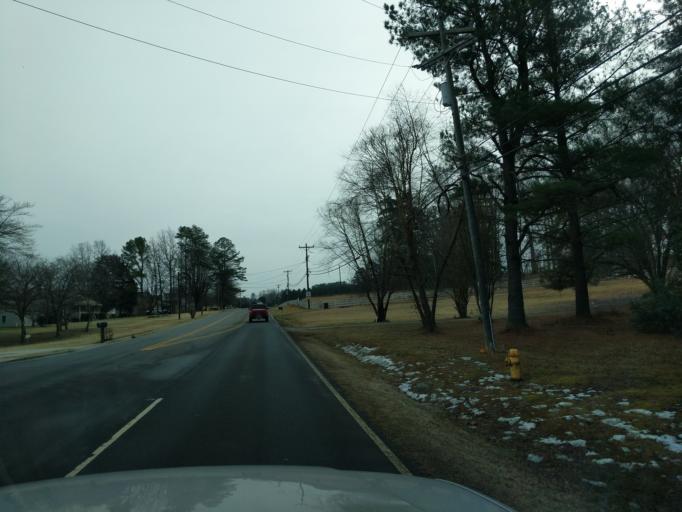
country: US
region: North Carolina
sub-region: Mecklenburg County
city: Huntersville
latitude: 35.3220
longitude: -80.8984
